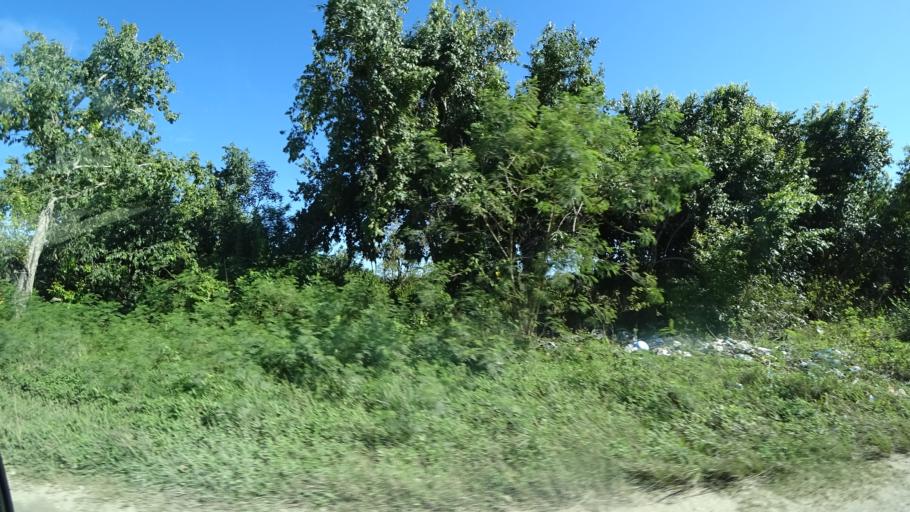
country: BZ
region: Belize
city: Belize City
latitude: 17.5765
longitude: -88.3400
